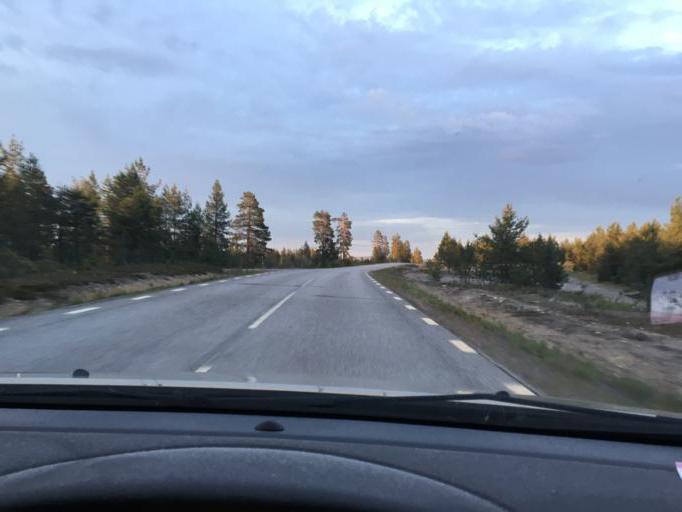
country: SE
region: Norrbotten
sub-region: Kalix Kommun
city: Toere
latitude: 66.0558
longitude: 22.4517
